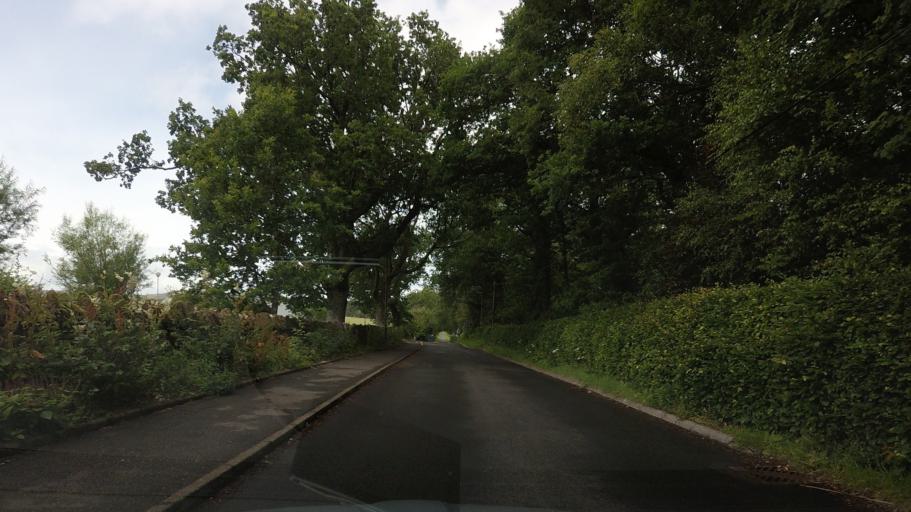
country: GB
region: Scotland
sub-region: Stirling
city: Killearn
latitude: 56.0693
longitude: -4.4513
